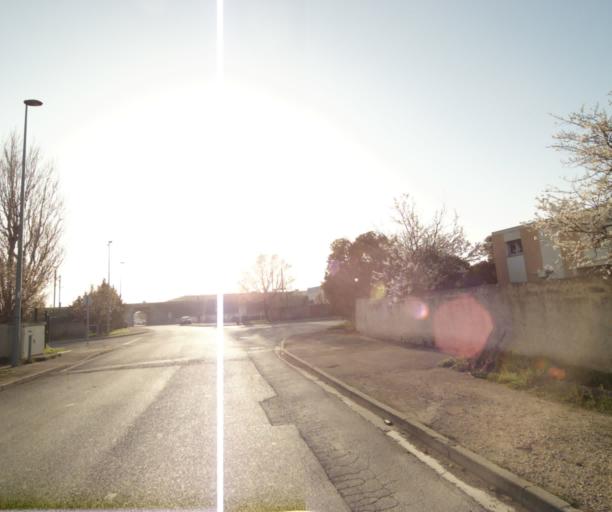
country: FR
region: Provence-Alpes-Cote d'Azur
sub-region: Departement des Bouches-du-Rhone
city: Saint-Victoret
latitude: 43.4275
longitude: 5.2472
